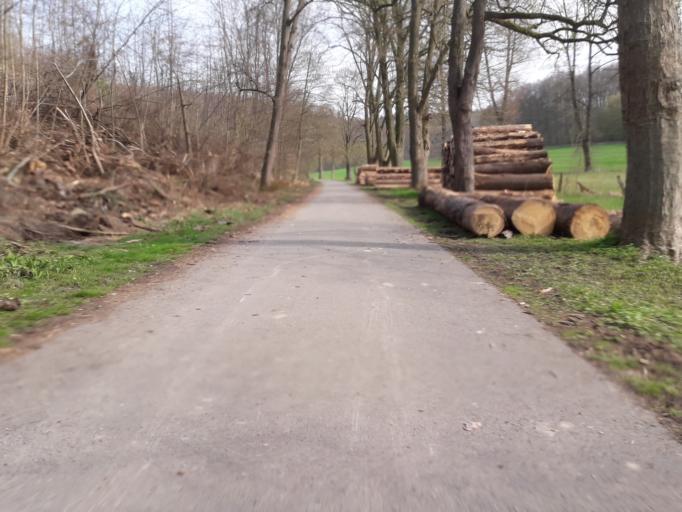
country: DE
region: North Rhine-Westphalia
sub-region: Regierungsbezirk Detmold
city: Paderborn
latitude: 51.6853
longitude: 8.7855
